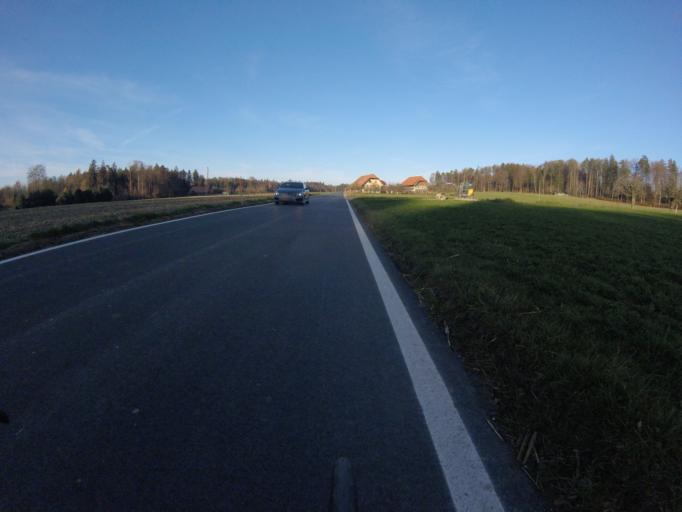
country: CH
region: Bern
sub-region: Bern-Mittelland District
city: Muhleberg
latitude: 46.9426
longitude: 7.2851
